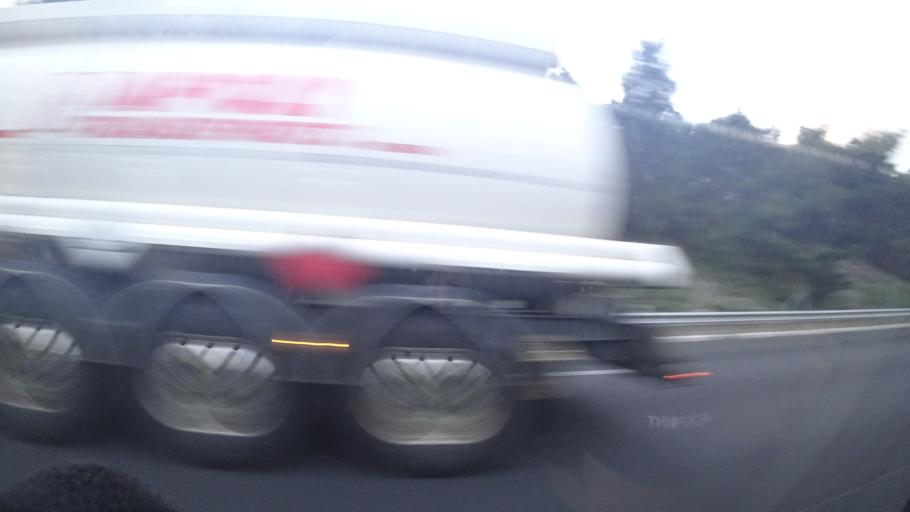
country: FR
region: Languedoc-Roussillon
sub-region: Departement de l'Aude
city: Peyriac-de-Mer
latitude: 43.1306
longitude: 2.9654
